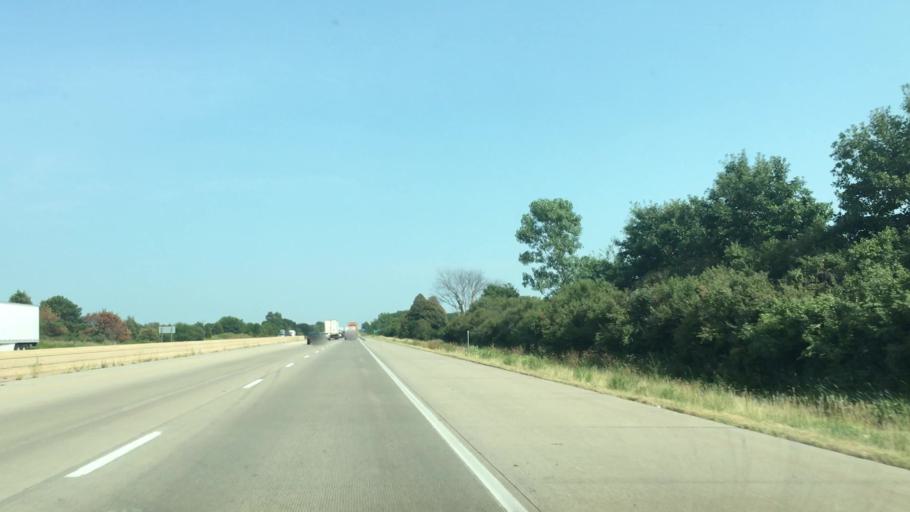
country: US
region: Iowa
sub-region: Johnson County
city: Iowa City
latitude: 41.6815
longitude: -91.4729
